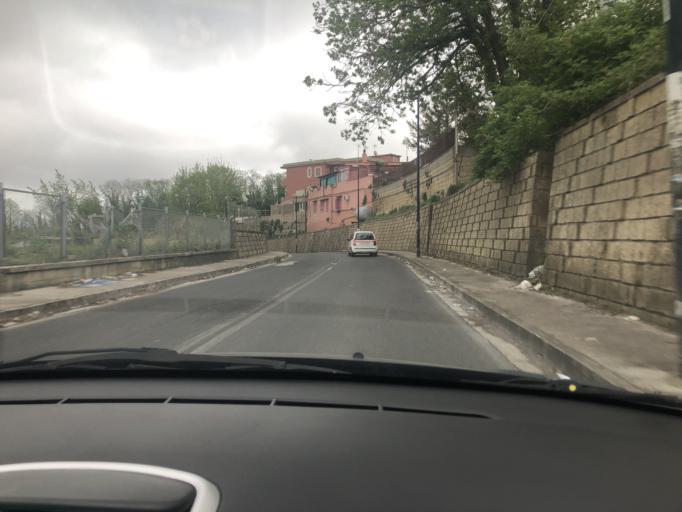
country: IT
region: Campania
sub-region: Provincia di Napoli
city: Torre Caracciolo
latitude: 40.8640
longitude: 14.1912
